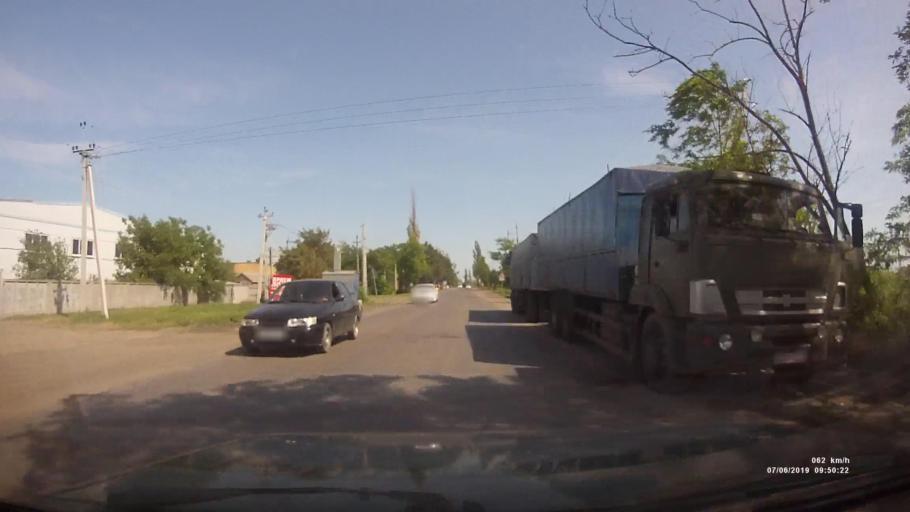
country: RU
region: Rostov
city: Azov
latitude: 47.0790
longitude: 39.4375
